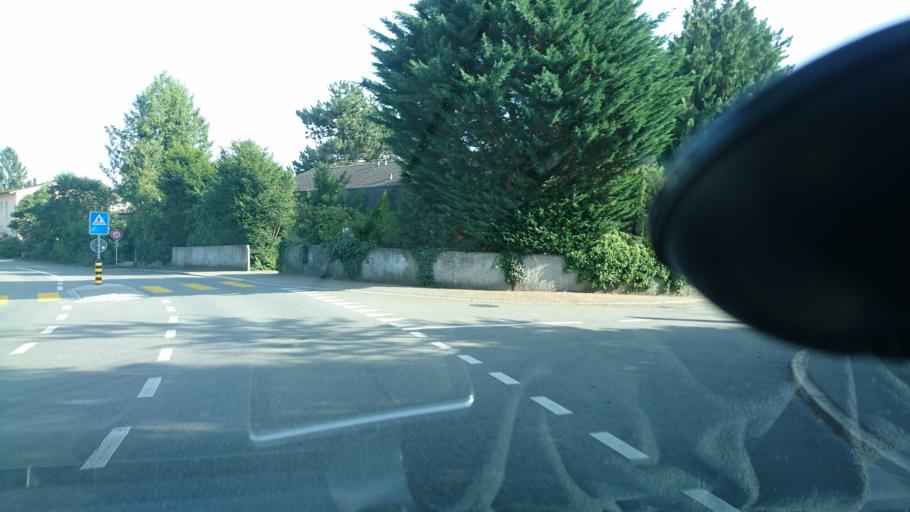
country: CH
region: Bern
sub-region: Bern-Mittelland District
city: Zollikofen
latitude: 46.9988
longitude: 7.4443
